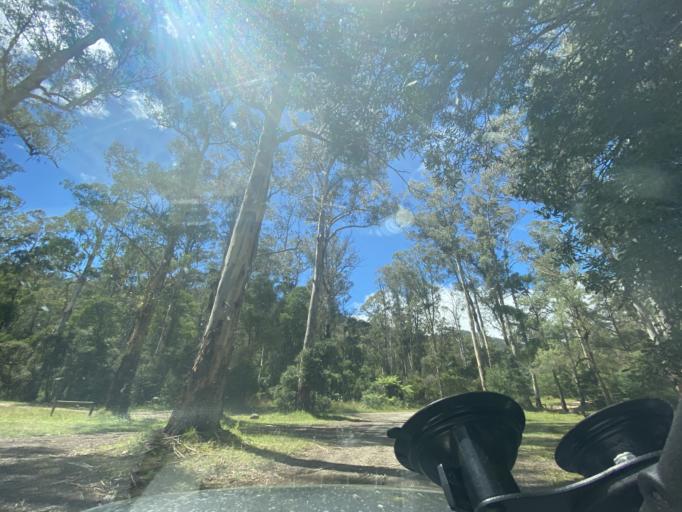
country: AU
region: Victoria
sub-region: Yarra Ranges
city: Millgrove
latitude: -37.5222
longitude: 146.0584
